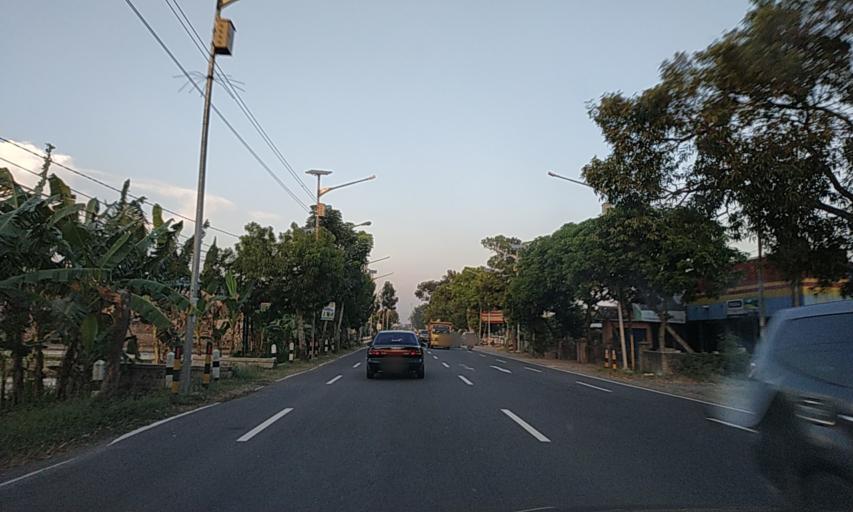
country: ID
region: Daerah Istimewa Yogyakarta
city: Srandakan
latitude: -7.8916
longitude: 110.1250
